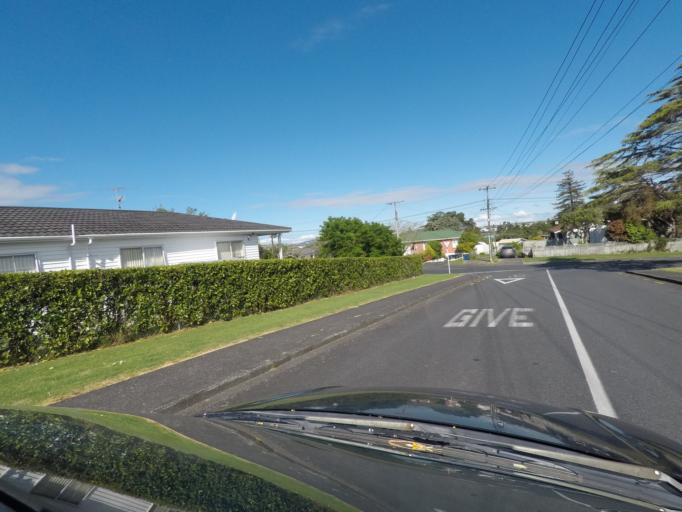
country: NZ
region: Auckland
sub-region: Auckland
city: Rosebank
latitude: -36.8665
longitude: 174.6511
